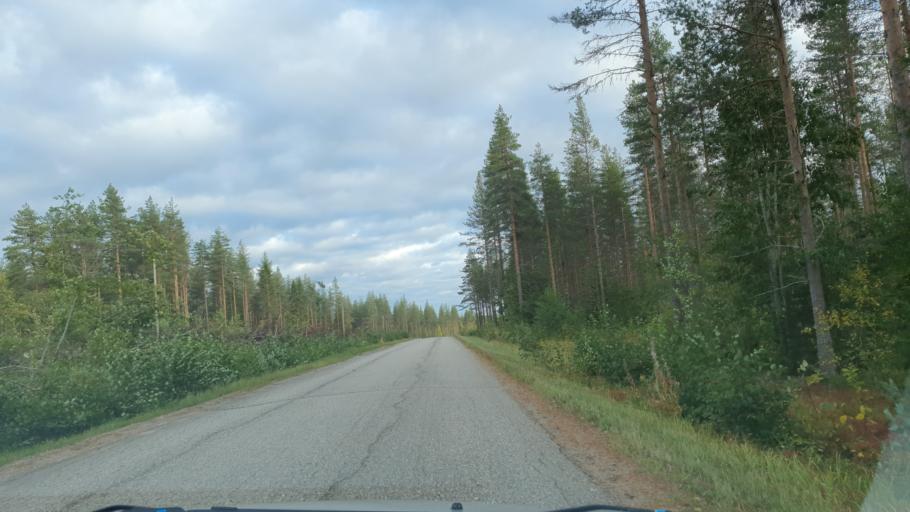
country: FI
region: North Karelia
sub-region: Pielisen Karjala
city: Lieksa
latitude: 63.9214
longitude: 30.1534
